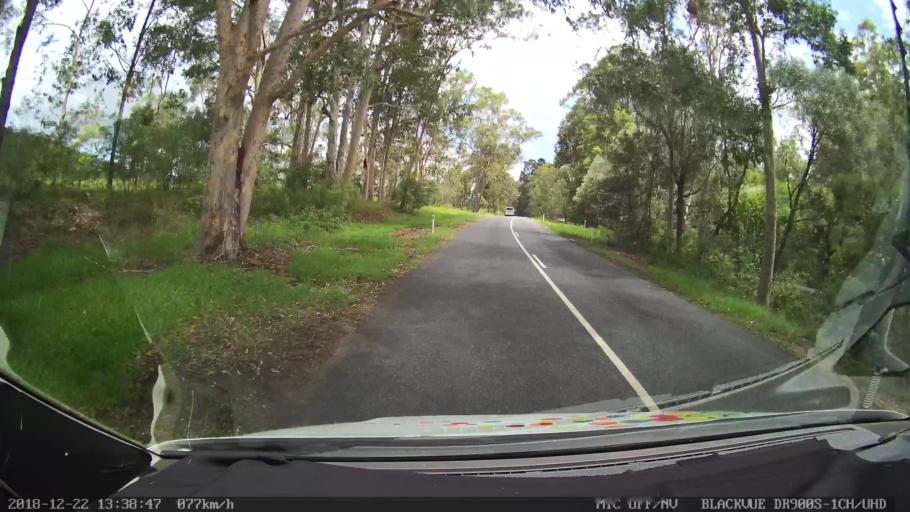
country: AU
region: New South Wales
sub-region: Clarence Valley
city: Coutts Crossing
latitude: -29.9039
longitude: 152.7862
